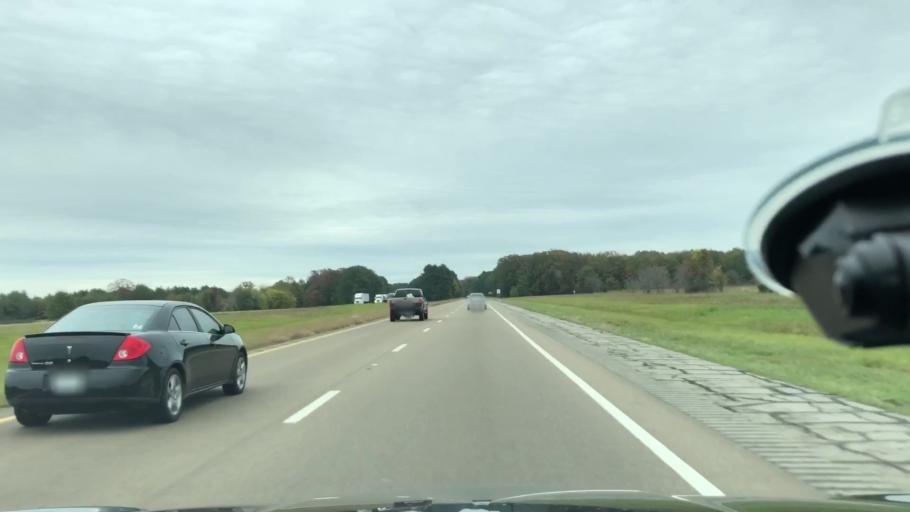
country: US
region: Texas
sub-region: Morris County
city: Naples
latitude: 33.2954
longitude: -94.7275
